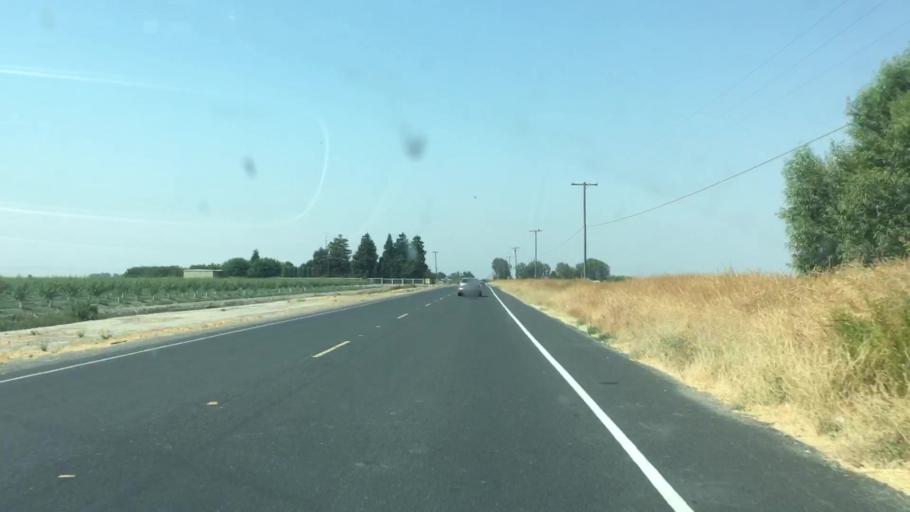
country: US
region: California
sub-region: San Joaquin County
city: Tracy
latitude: 37.8510
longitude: -121.4171
